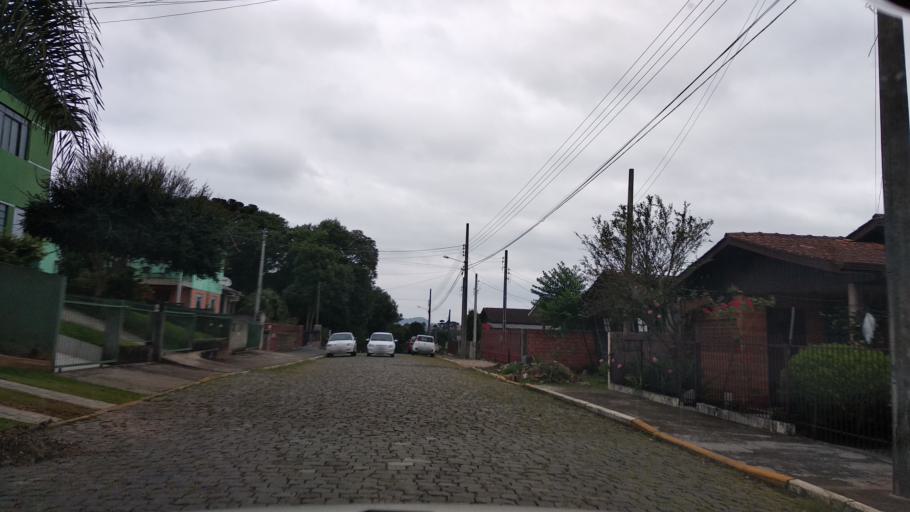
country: BR
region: Santa Catarina
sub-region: Videira
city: Videira
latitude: -26.9864
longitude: -51.1719
